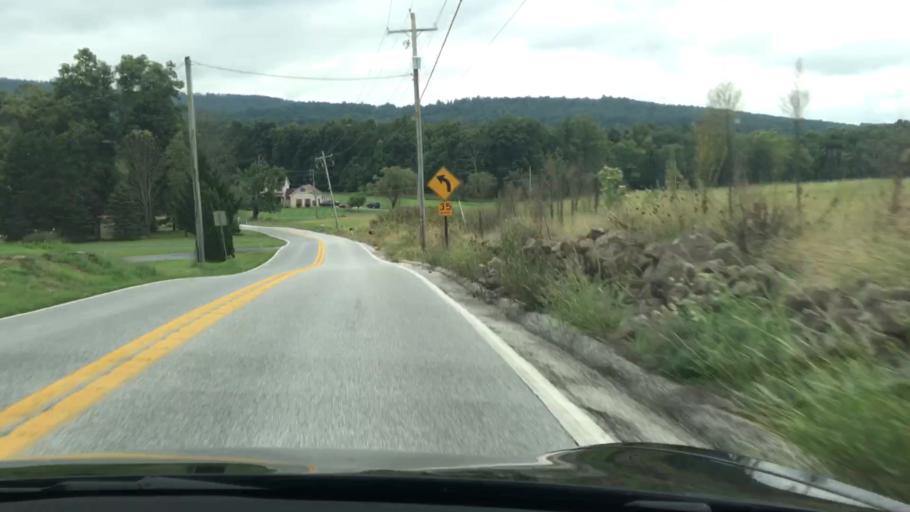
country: US
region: Pennsylvania
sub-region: York County
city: Dillsburg
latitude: 40.1308
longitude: -76.9616
